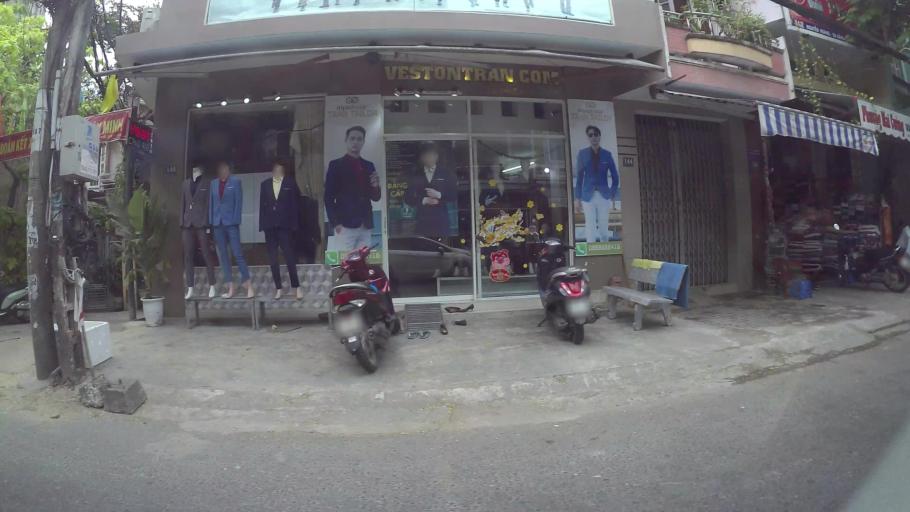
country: VN
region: Da Nang
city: Da Nang
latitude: 16.0620
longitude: 108.2139
